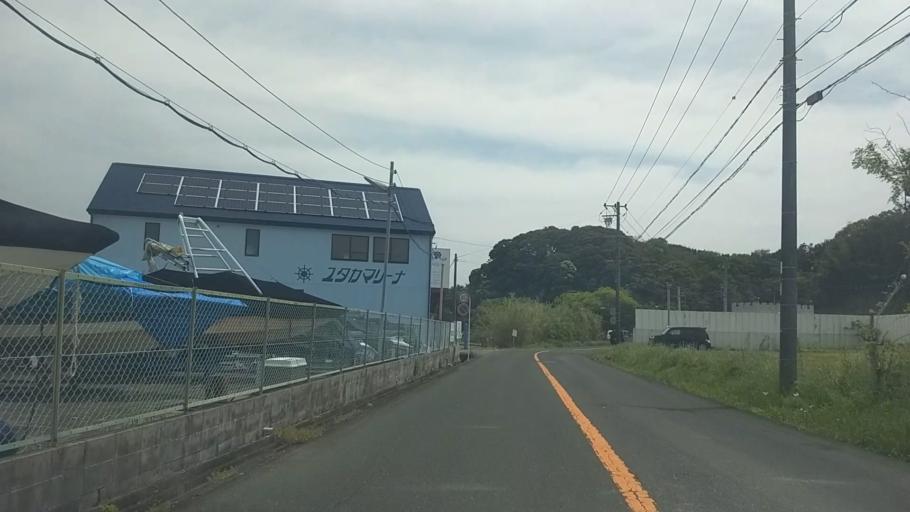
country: JP
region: Shizuoka
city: Kosai-shi
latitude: 34.7542
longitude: 137.5136
